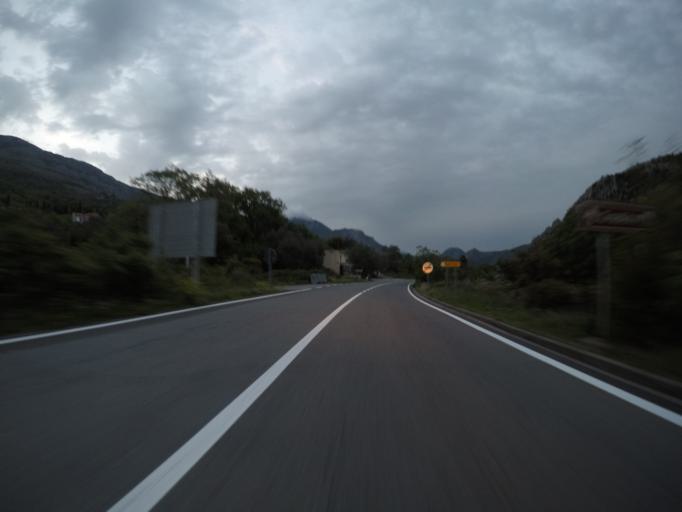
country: ME
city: Petrovac na Moru
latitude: 42.2036
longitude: 18.9584
